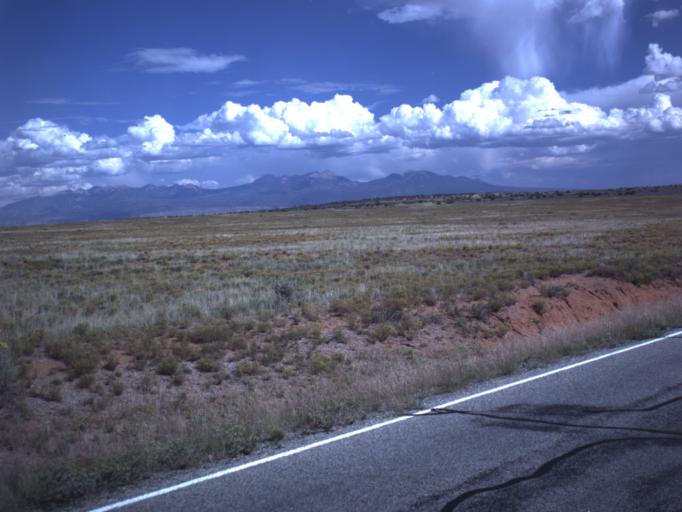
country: US
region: Utah
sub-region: Grand County
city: Moab
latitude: 38.5433
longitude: -109.7603
